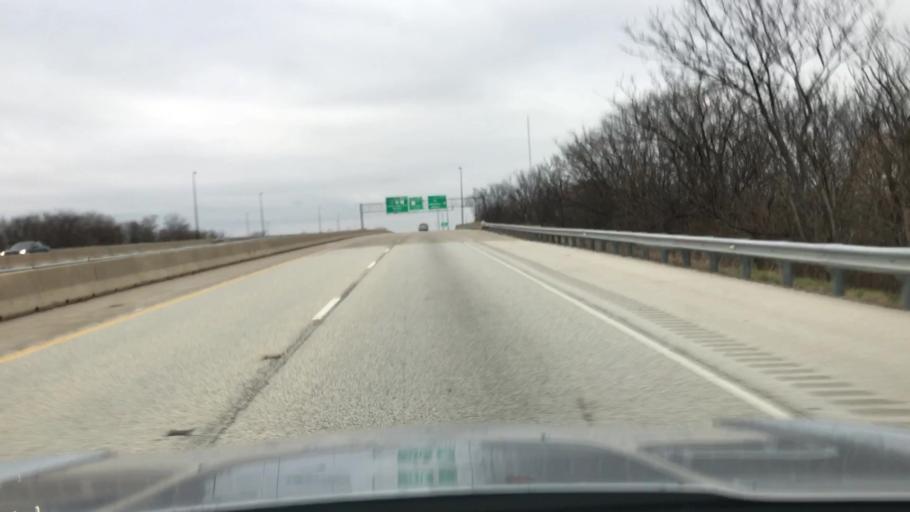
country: US
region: Illinois
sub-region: Sangamon County
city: Grandview
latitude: 39.8367
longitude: -89.5938
